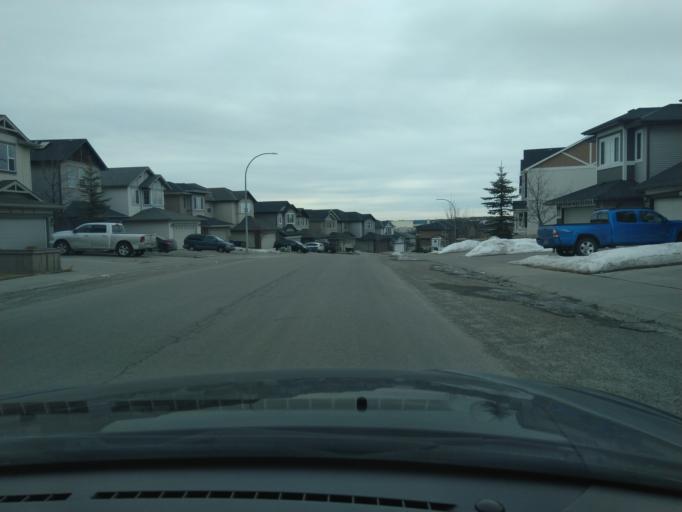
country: CA
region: Alberta
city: Calgary
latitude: 51.1645
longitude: -114.0975
